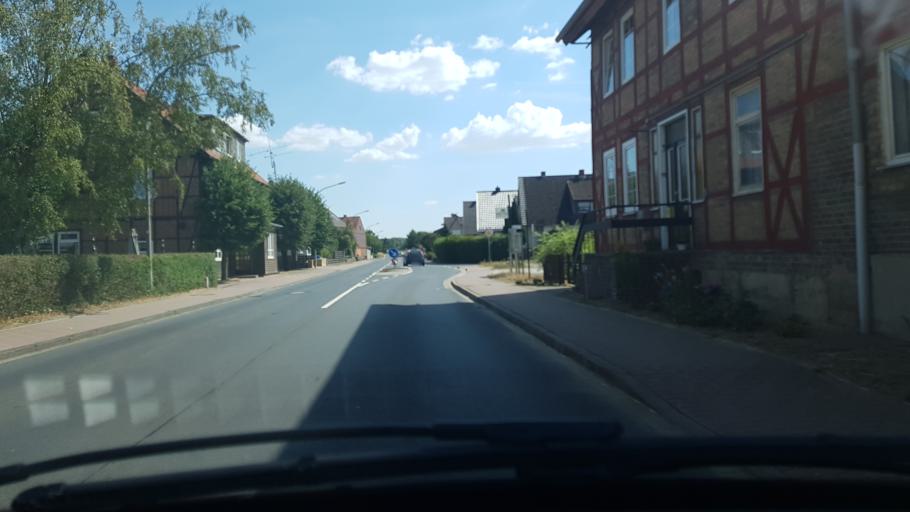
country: DE
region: Lower Saxony
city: Lehre
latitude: 52.3071
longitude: 10.6584
